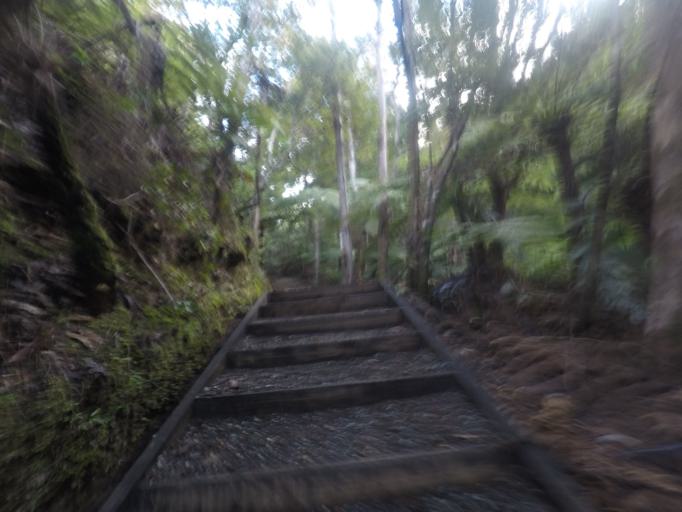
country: NZ
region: Auckland
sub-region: Auckland
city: Titirangi
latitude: -37.0028
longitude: 174.5549
